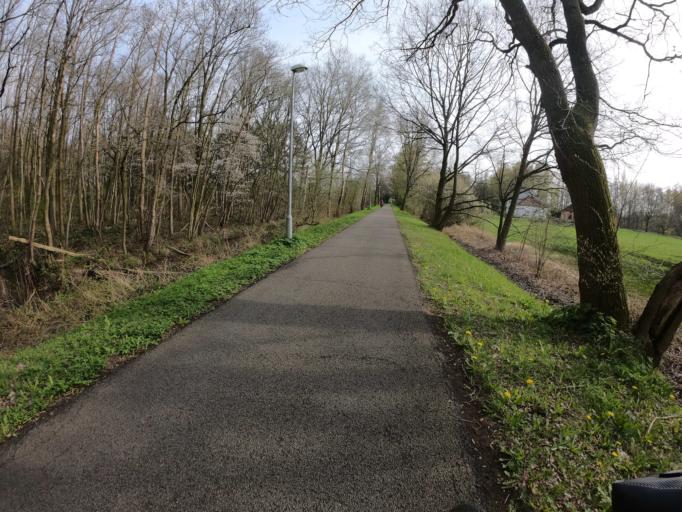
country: BE
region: Flanders
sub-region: Provincie Vlaams-Brabant
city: Aarschot
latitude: 51.0121
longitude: 4.8320
